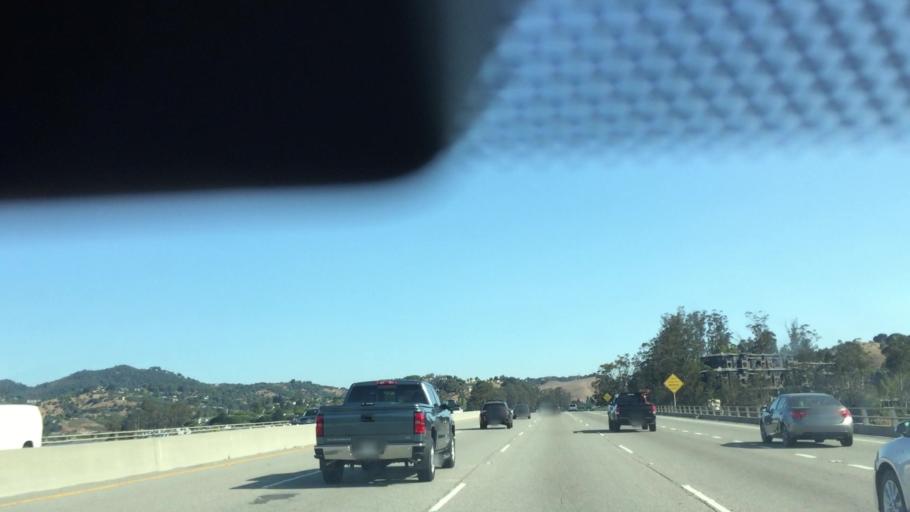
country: US
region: California
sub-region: Marin County
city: Strawberry
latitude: 37.8828
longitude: -122.5164
